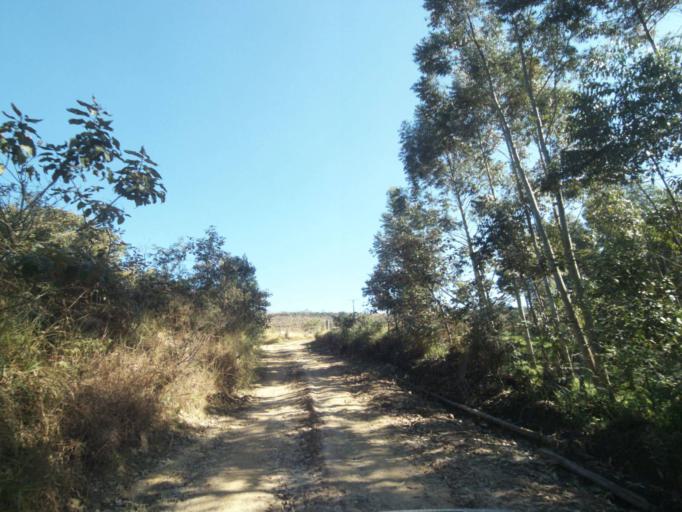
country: BR
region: Parana
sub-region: Tibagi
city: Tibagi
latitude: -24.5756
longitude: -50.4774
